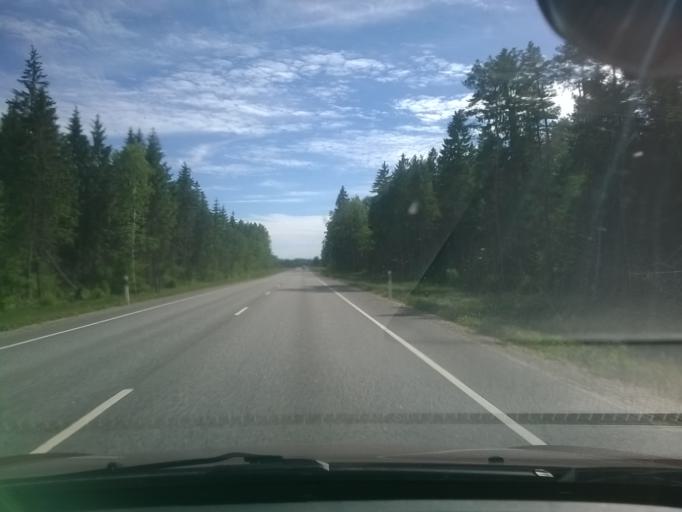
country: EE
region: Jaervamaa
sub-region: Paide linn
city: Paide
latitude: 58.9489
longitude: 25.6474
